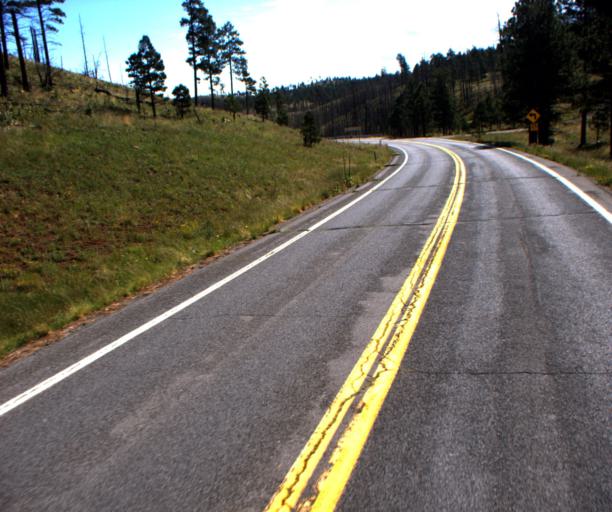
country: US
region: Arizona
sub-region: Apache County
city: Eagar
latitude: 34.0508
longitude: -109.3497
